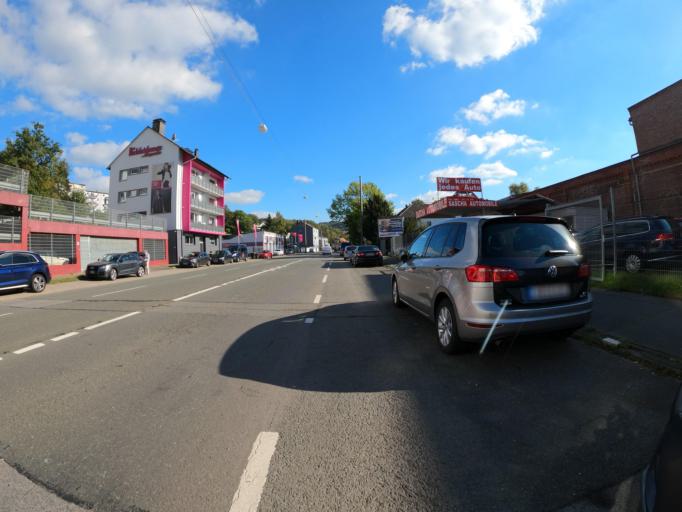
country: DE
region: North Rhine-Westphalia
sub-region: Regierungsbezirk Dusseldorf
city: Wuppertal
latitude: 51.2721
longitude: 7.2303
